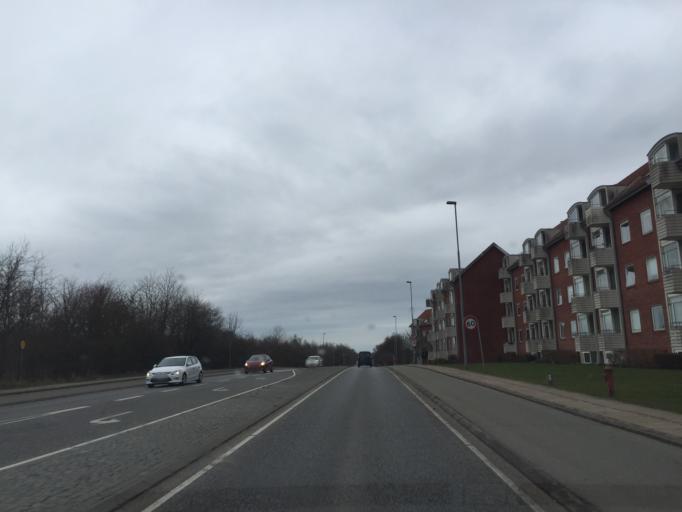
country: DK
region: South Denmark
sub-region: Odense Kommune
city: Odense
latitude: 55.3992
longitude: 10.3397
